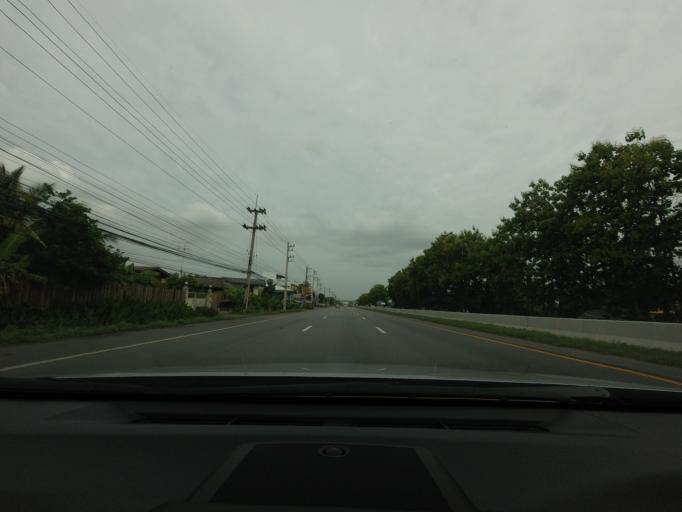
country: TH
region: Phetchaburi
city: Khao Yoi
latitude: 13.1994
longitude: 99.8302
